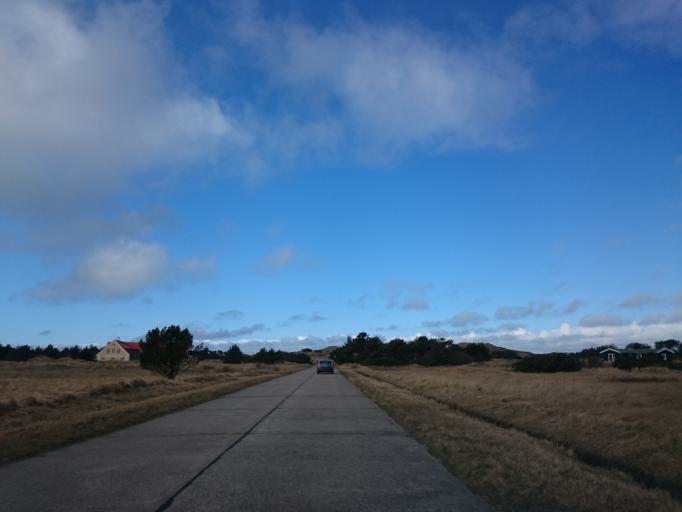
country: DK
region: North Denmark
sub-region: Frederikshavn Kommune
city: Strandby
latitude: 57.6614
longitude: 10.3947
